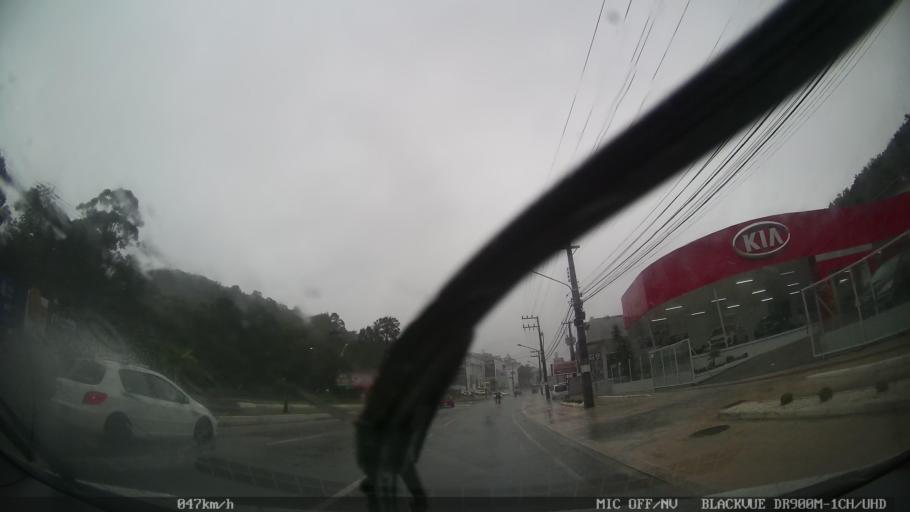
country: BR
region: Santa Catarina
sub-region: Balneario Camboriu
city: Balneario Camboriu
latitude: -26.9580
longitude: -48.6394
